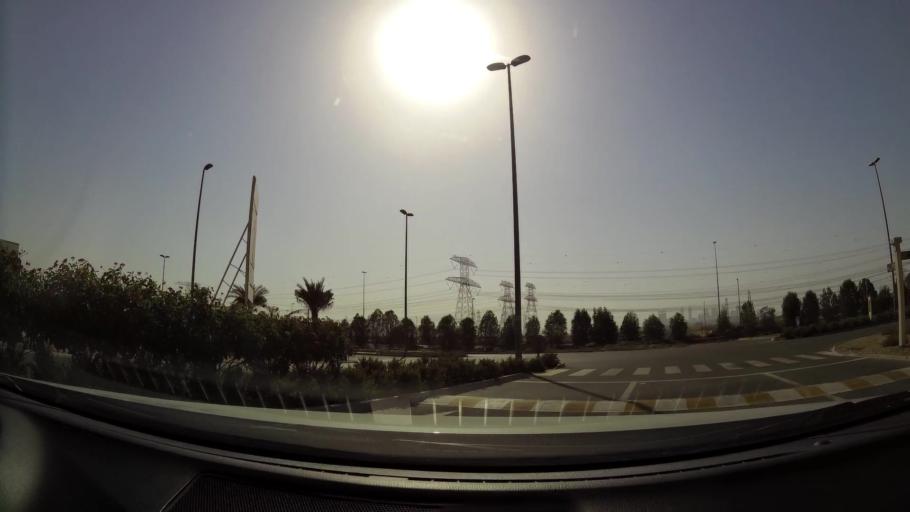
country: AE
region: Dubai
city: Dubai
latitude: 25.0700
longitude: 55.2061
